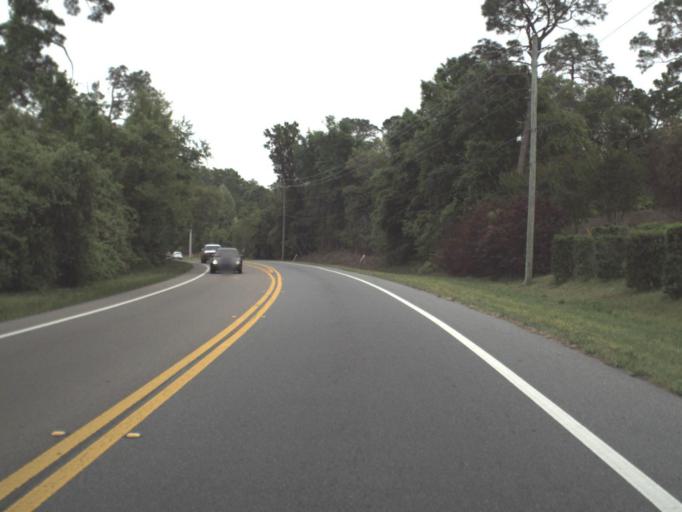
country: US
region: Florida
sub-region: Escambia County
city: Ferry Pass
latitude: 30.5263
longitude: -87.1857
